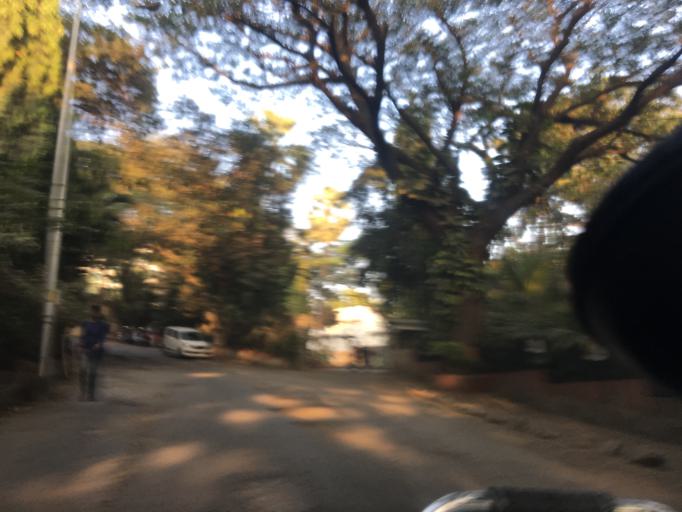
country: IN
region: Maharashtra
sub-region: Mumbai Suburban
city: Powai
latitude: 19.1319
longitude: 72.8982
